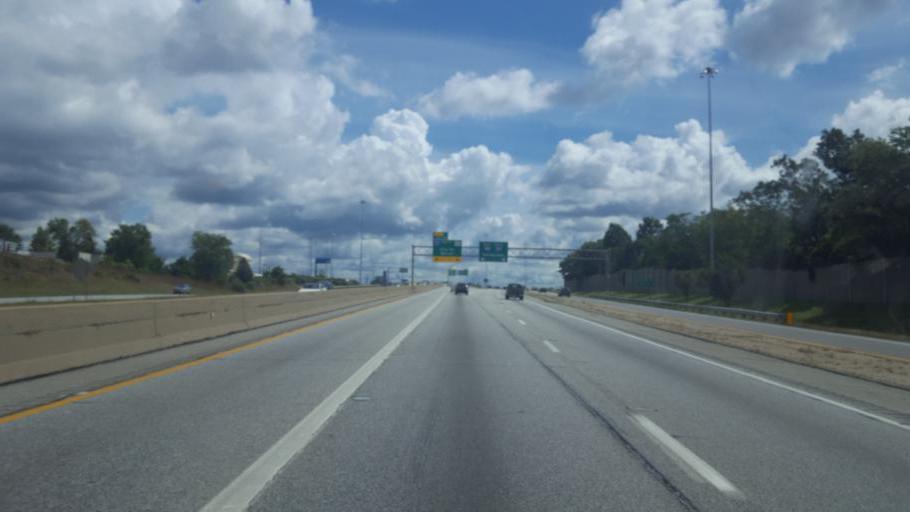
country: US
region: Ohio
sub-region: Cuyahoga County
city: Bedford Heights
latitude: 41.4246
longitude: -81.5346
